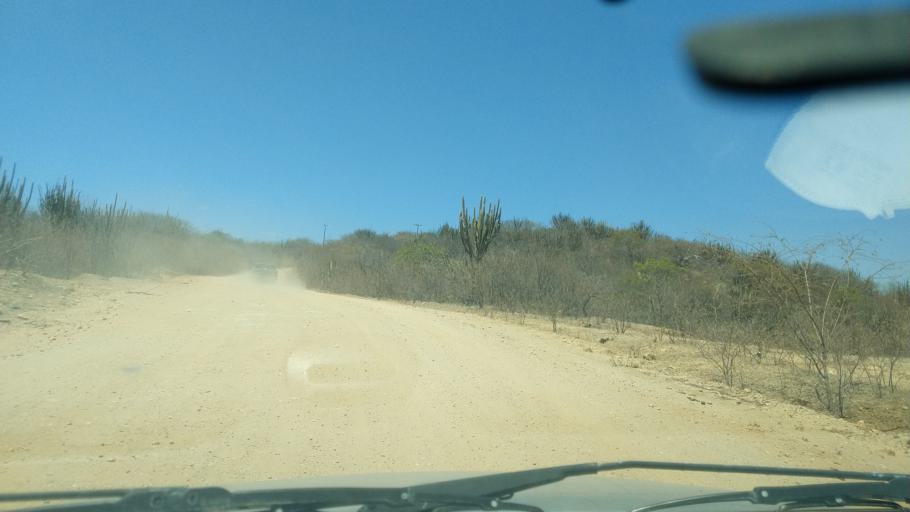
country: BR
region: Rio Grande do Norte
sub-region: Cerro Cora
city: Cerro Cora
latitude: -6.0102
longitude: -36.2814
